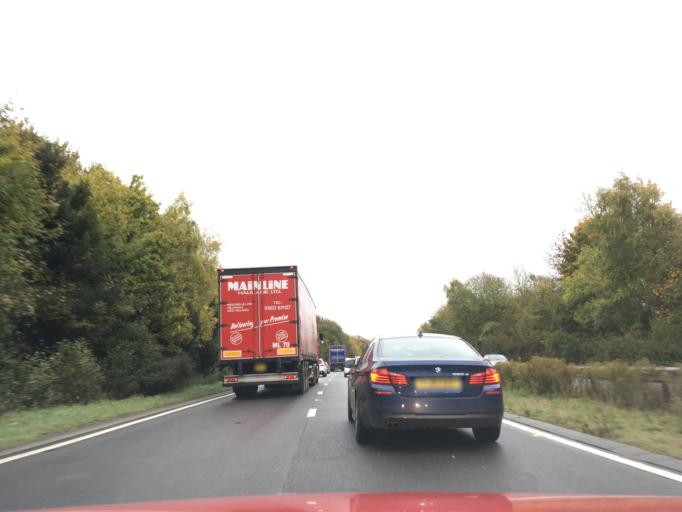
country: GB
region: England
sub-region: Hampshire
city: Kings Worthy
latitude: 51.0936
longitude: -1.3099
